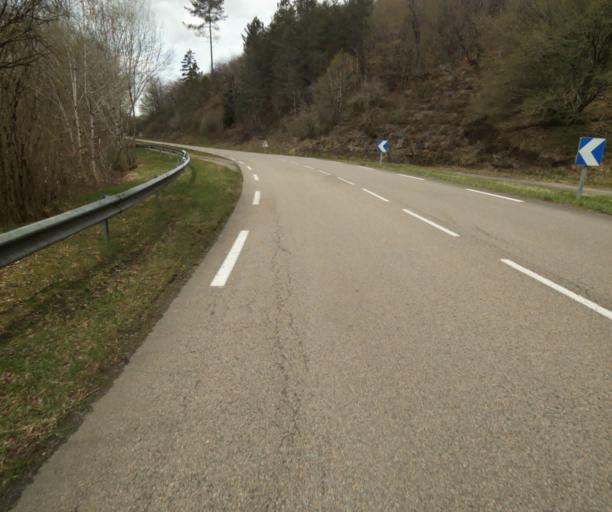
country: FR
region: Limousin
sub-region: Departement de la Correze
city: Sainte-Fortunade
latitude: 45.1835
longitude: 1.8480
